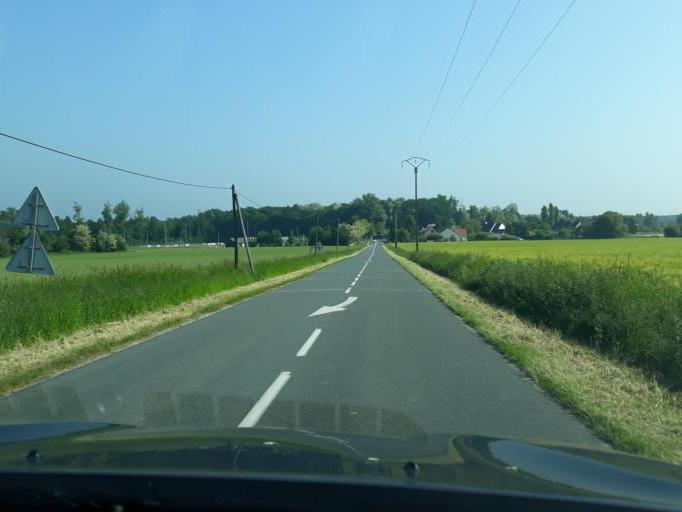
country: FR
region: Centre
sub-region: Departement du Loiret
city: Boigny-sur-Bionne
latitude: 47.9233
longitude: 2.0240
